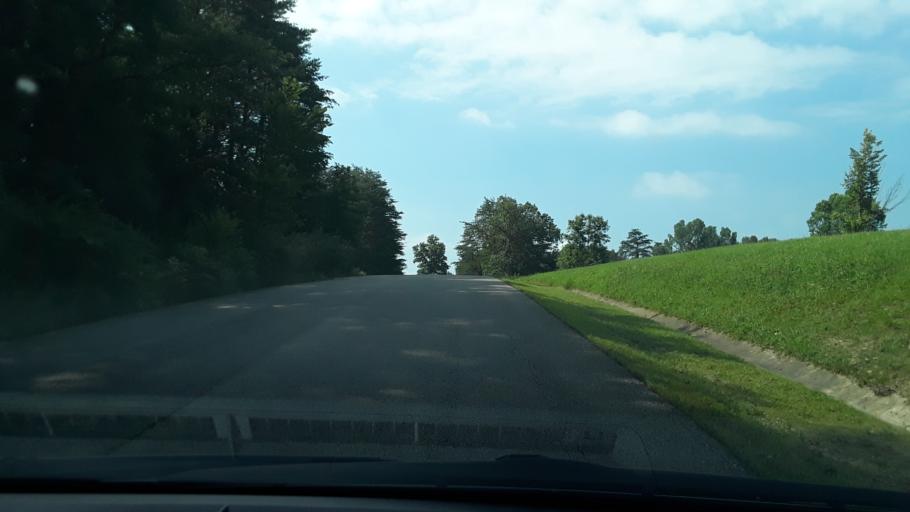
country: US
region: Indiana
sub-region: Clark County
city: Henryville
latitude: 38.4635
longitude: -85.8655
